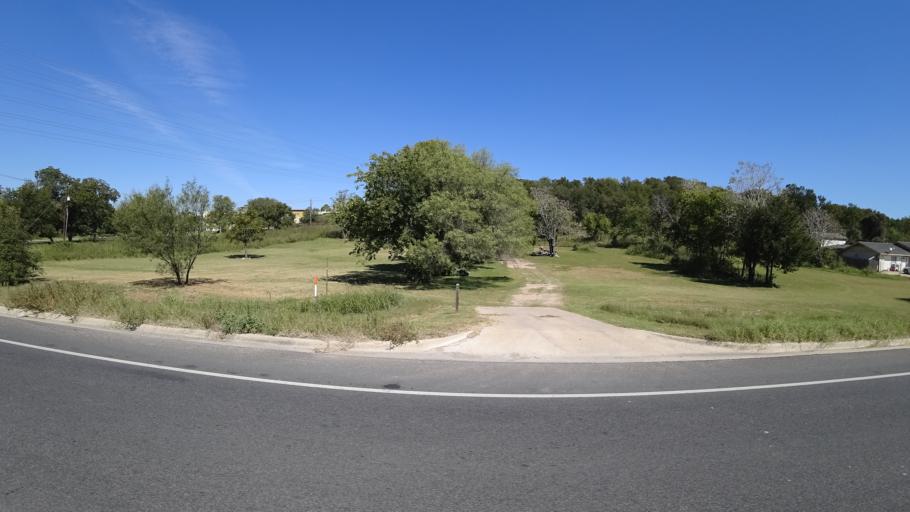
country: US
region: Texas
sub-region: Travis County
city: Hornsby Bend
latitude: 30.2805
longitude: -97.6470
